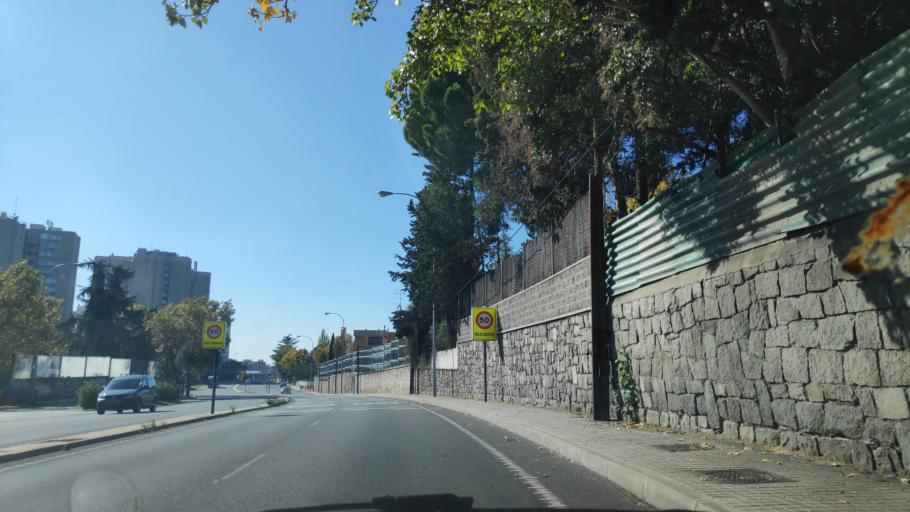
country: ES
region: Madrid
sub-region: Provincia de Madrid
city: Tetuan de las Victorias
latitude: 40.4868
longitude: -3.7077
